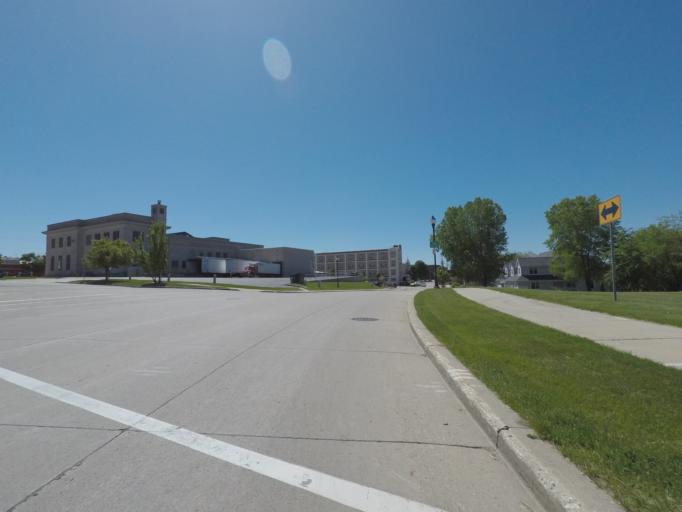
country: US
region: Wisconsin
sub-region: Sheboygan County
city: Sheboygan
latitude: 43.7510
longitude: -87.7160
